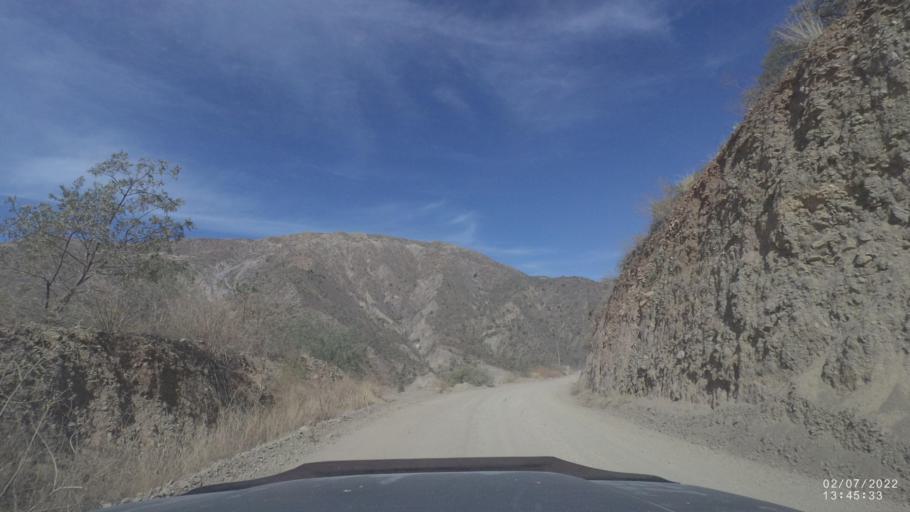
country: BO
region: Cochabamba
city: Irpa Irpa
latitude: -17.8090
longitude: -66.3650
